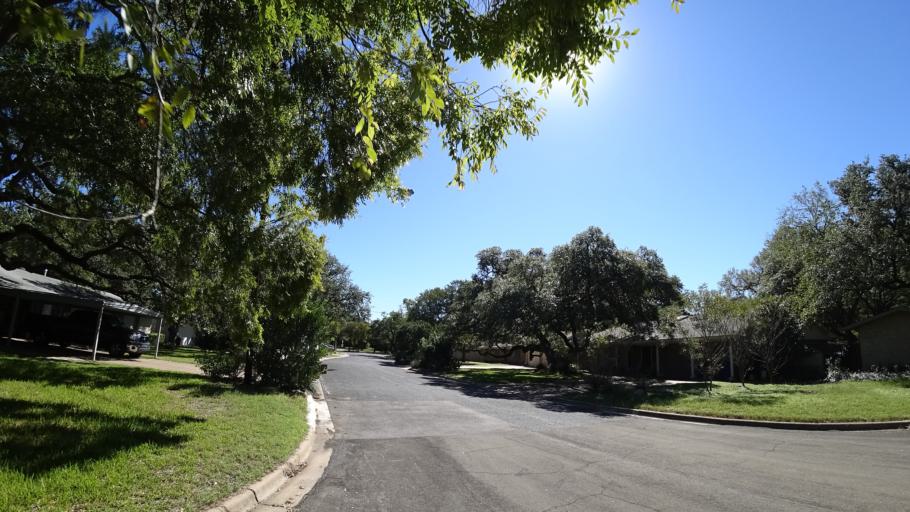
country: US
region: Texas
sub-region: Travis County
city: Rollingwood
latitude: 30.2205
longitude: -97.7953
